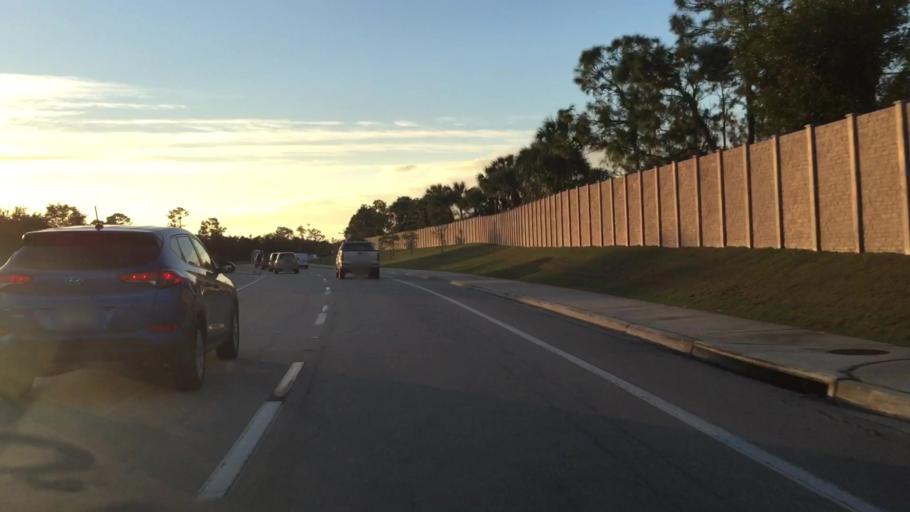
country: US
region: Florida
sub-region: Lee County
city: Gateway
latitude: 26.5953
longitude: -81.7858
